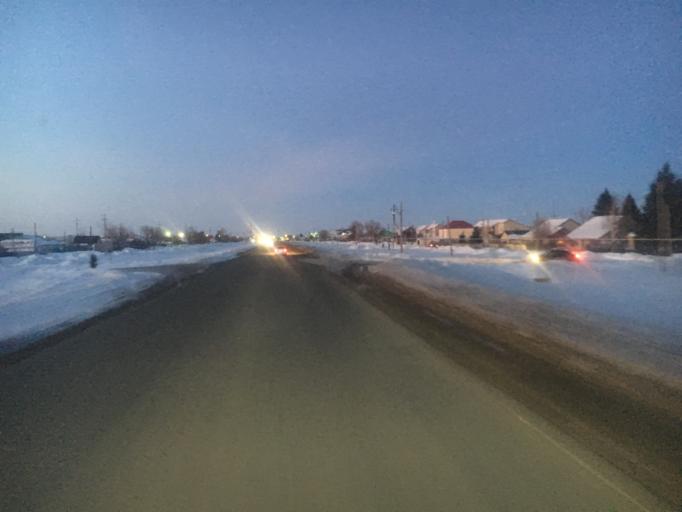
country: KZ
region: Batys Qazaqstan
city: Oral
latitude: 51.1412
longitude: 51.4864
